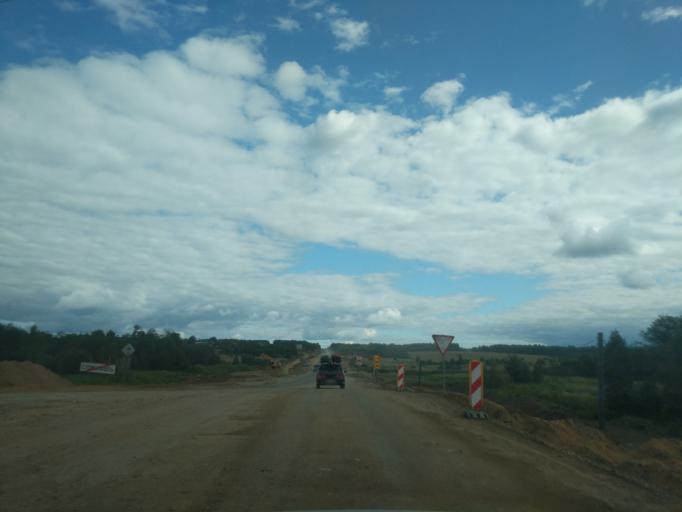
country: RU
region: Kostroma
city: Sudislavl'
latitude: 57.8772
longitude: 41.7283
